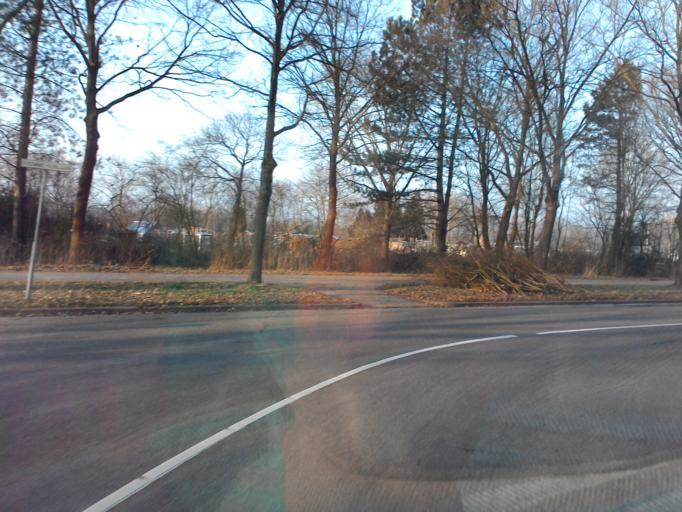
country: NL
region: Utrecht
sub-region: Gemeente Bunnik
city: Bunnik
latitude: 52.0876
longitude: 5.2075
